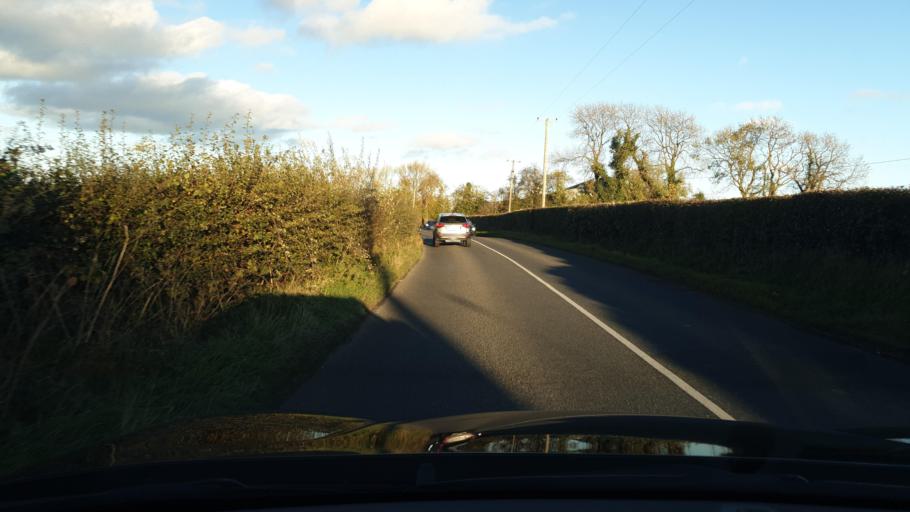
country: IE
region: Leinster
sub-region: Lu
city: Drogheda
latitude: 53.6936
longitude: -6.3360
